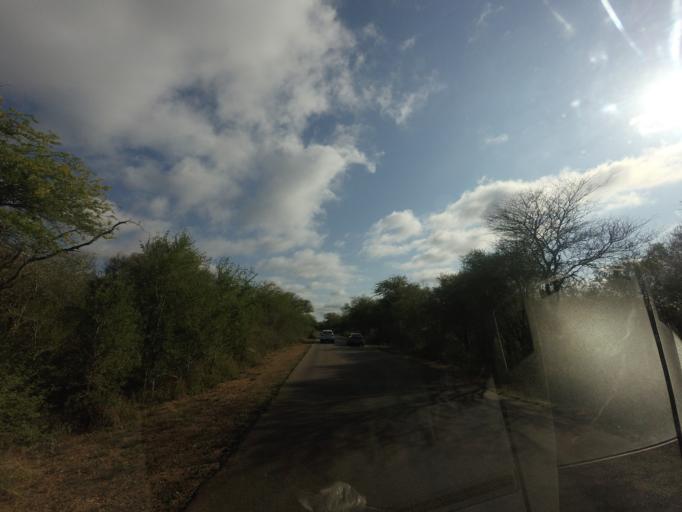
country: ZA
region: Mpumalanga
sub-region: Ehlanzeni District
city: Komatipoort
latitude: -25.2221
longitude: 31.8622
